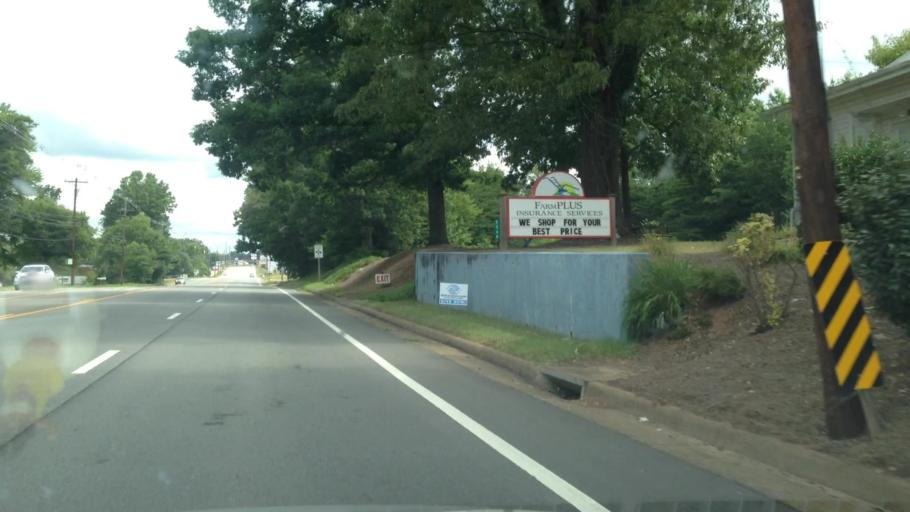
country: US
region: Virginia
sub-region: Pittsylvania County
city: Mount Hermon
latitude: 36.6806
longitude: -79.3723
